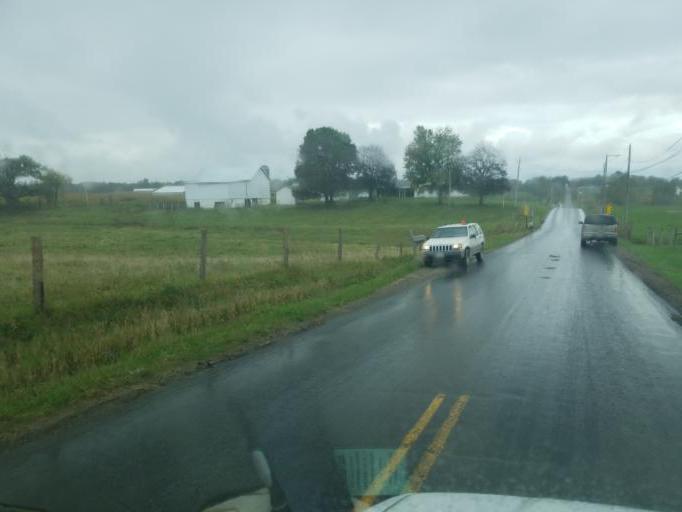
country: US
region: Ohio
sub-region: Wayne County
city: Shreve
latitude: 40.6681
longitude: -82.0228
